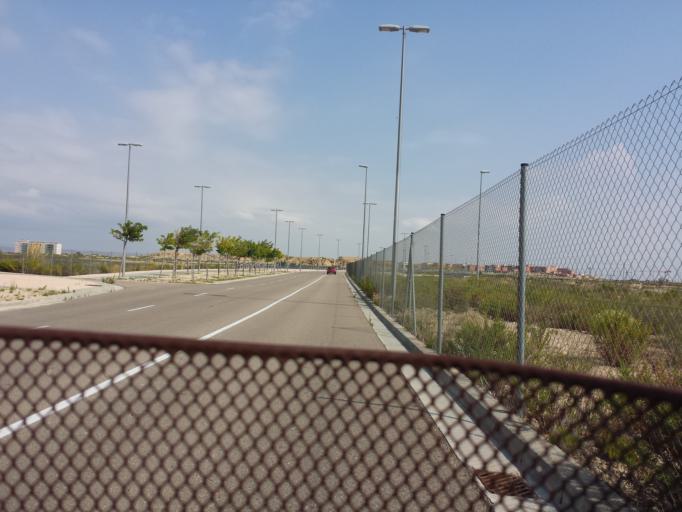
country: ES
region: Aragon
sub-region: Provincia de Zaragoza
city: Montecanal
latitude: 41.6281
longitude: -0.9556
